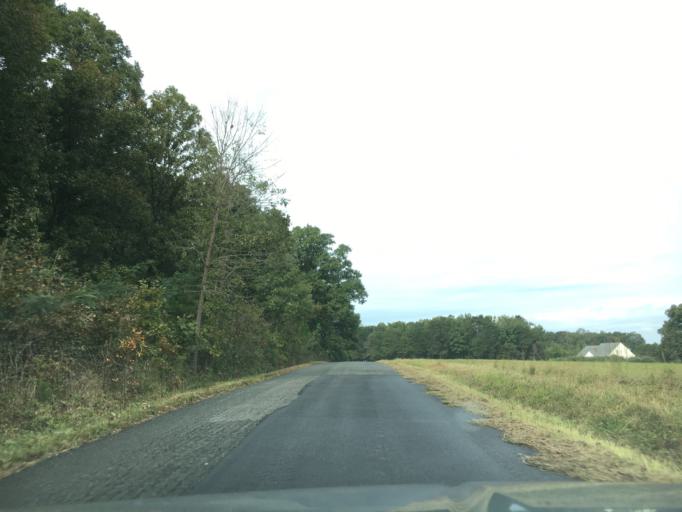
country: US
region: Virginia
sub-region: Goochland County
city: Goochland
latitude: 37.7080
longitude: -77.8401
